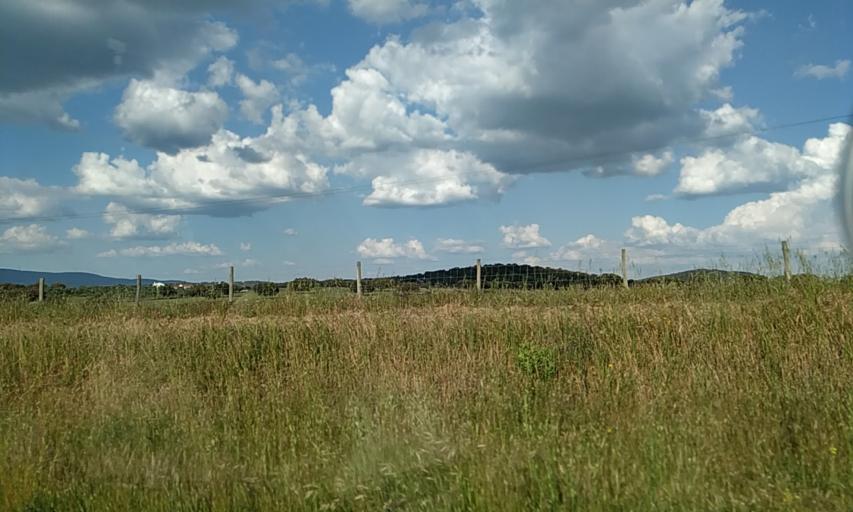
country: PT
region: Portalegre
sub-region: Portalegre
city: Urra
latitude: 39.2036
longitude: -7.4585
